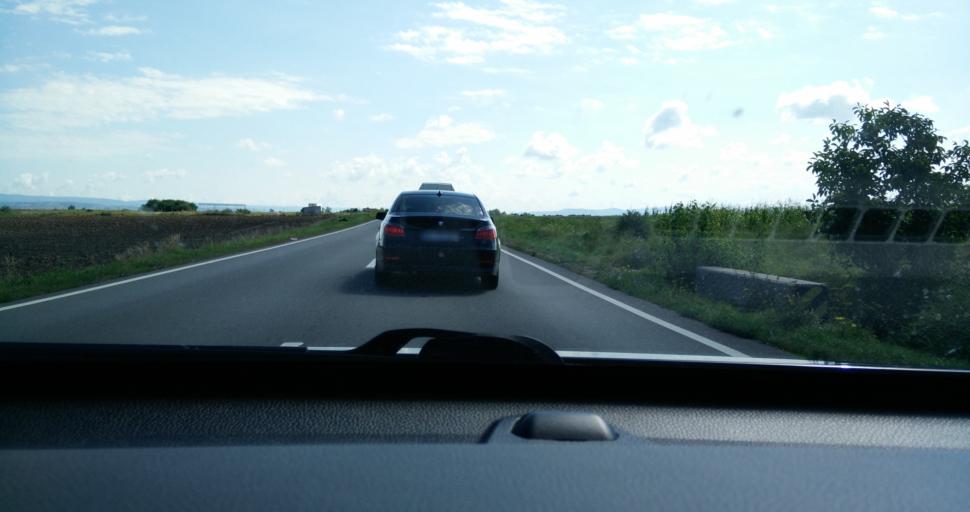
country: RO
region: Bihor
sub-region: Comuna Osorheiu
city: Osorheiu
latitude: 47.0543
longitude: 22.0829
